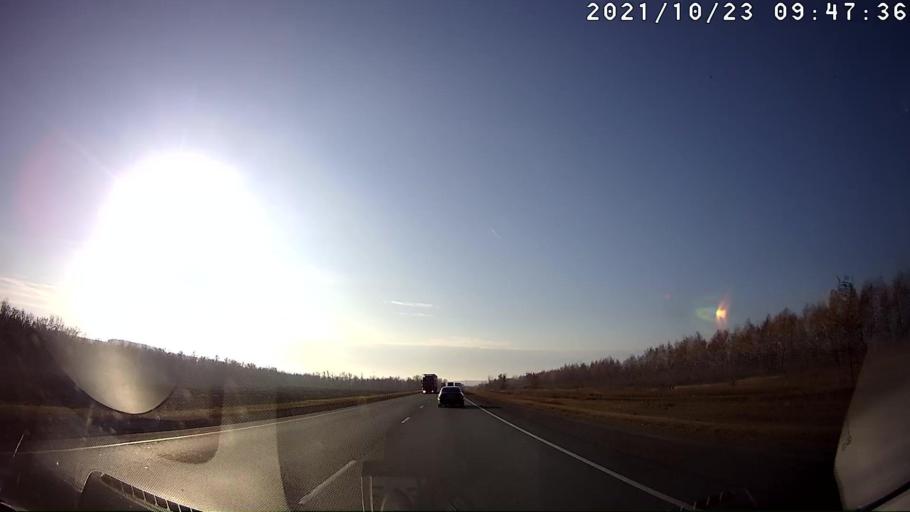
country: RU
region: Saratov
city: Sokolovyy
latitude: 51.5223
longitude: 45.8083
